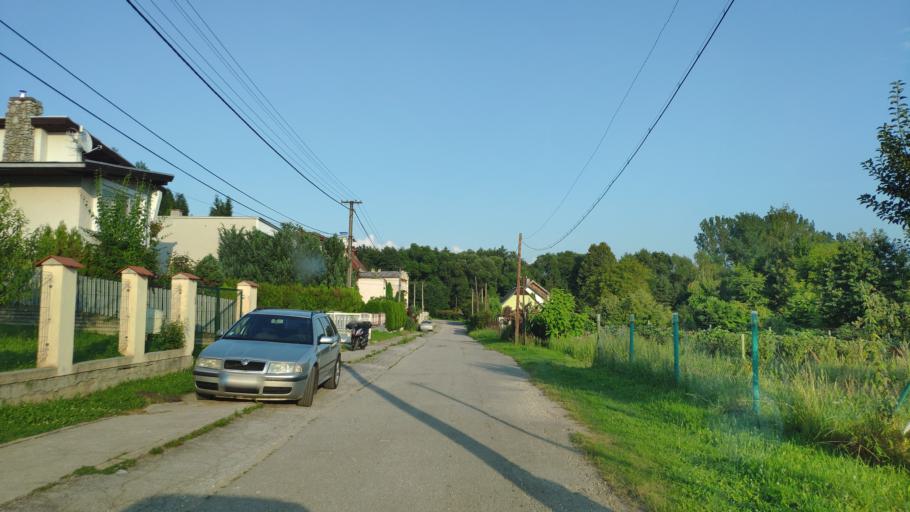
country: SK
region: Kosicky
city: Dobsina
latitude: 48.7198
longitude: 20.2760
